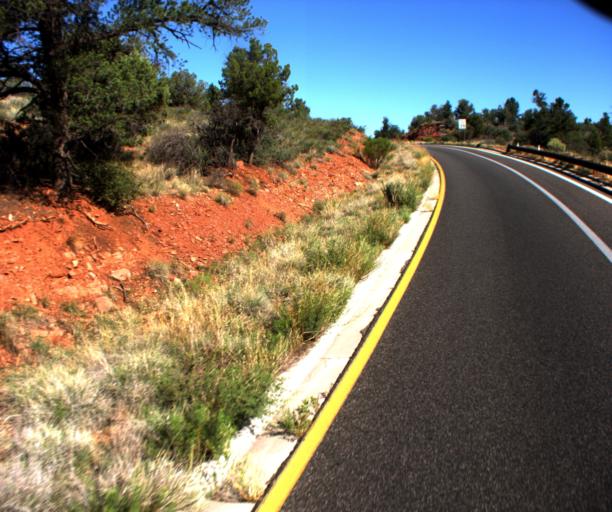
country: US
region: Arizona
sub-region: Yavapai County
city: Village of Oak Creek (Big Park)
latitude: 34.8208
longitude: -111.7725
